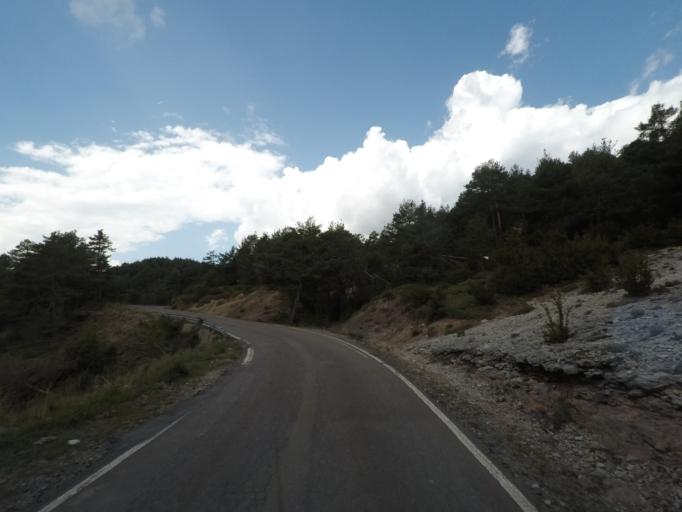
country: ES
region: Aragon
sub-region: Provincia de Huesca
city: Fiscal
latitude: 42.4064
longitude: -0.0852
